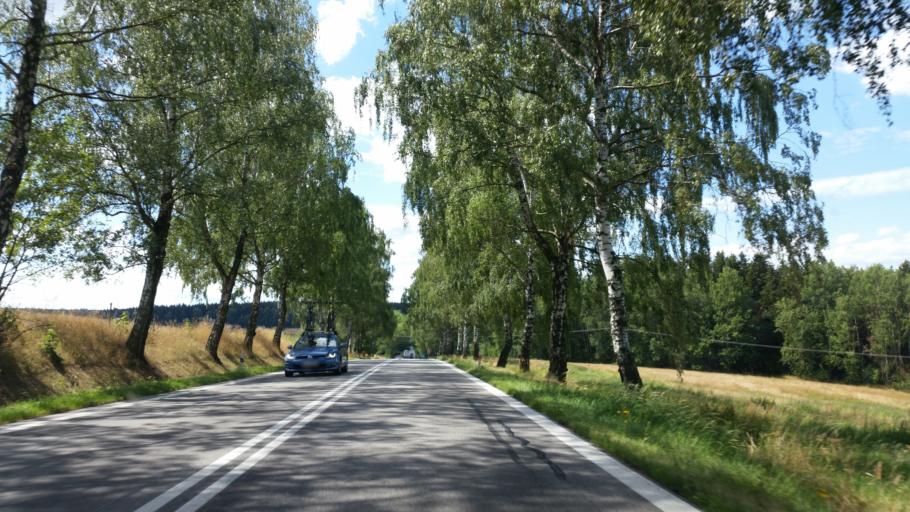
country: CZ
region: Vysocina
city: Pacov
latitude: 49.4231
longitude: 14.9843
